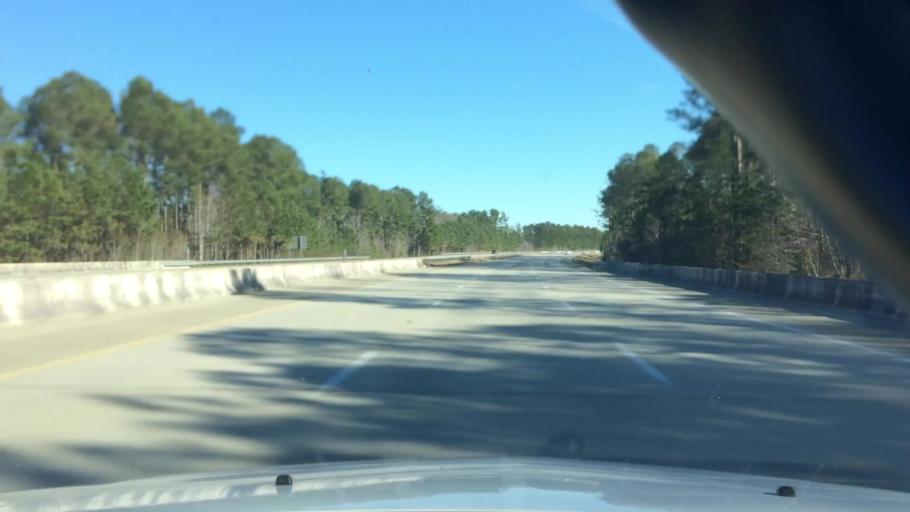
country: US
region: South Carolina
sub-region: Horry County
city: North Myrtle Beach
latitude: 33.8644
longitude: -78.6940
